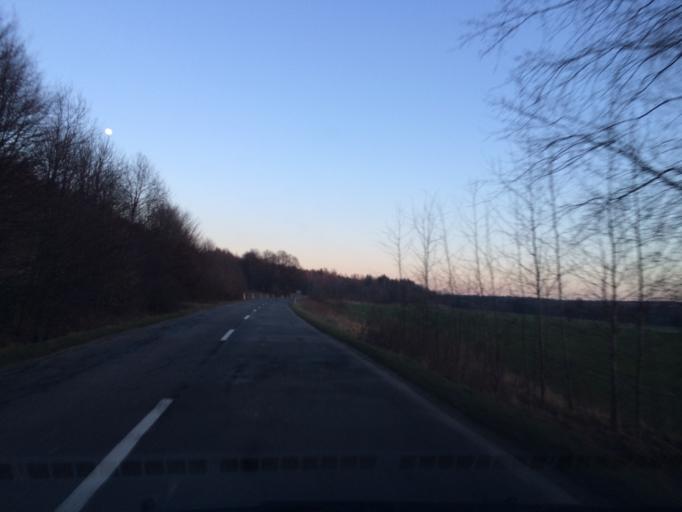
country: PL
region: Lower Silesian Voivodeship
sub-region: Powiat lwowecki
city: Lwowek Slaski
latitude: 51.1200
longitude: 15.6348
